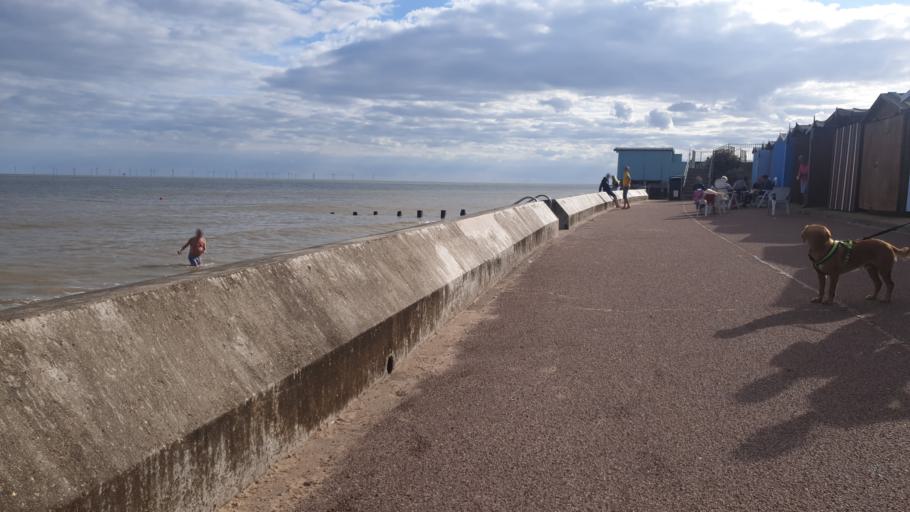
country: GB
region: England
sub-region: Essex
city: Frinton-on-Sea
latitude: 51.8238
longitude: 1.2423
